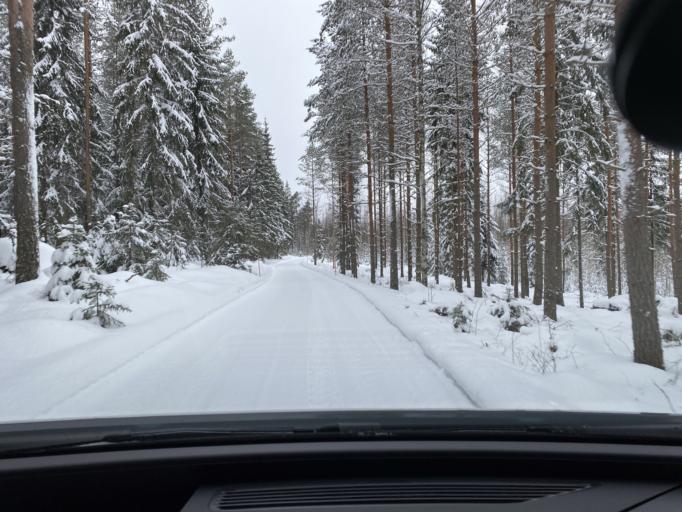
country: FI
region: Pirkanmaa
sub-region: Lounais-Pirkanmaa
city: Punkalaidun
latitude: 61.1342
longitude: 23.0959
